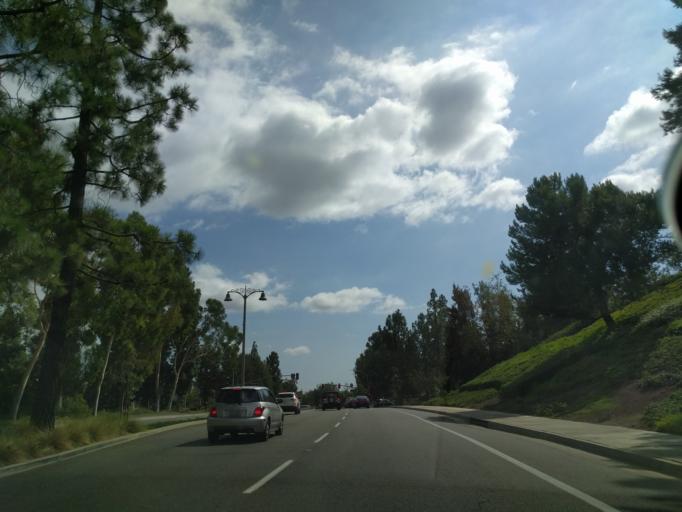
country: US
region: California
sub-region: Orange County
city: Mission Viejo
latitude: 33.6291
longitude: -117.6512
